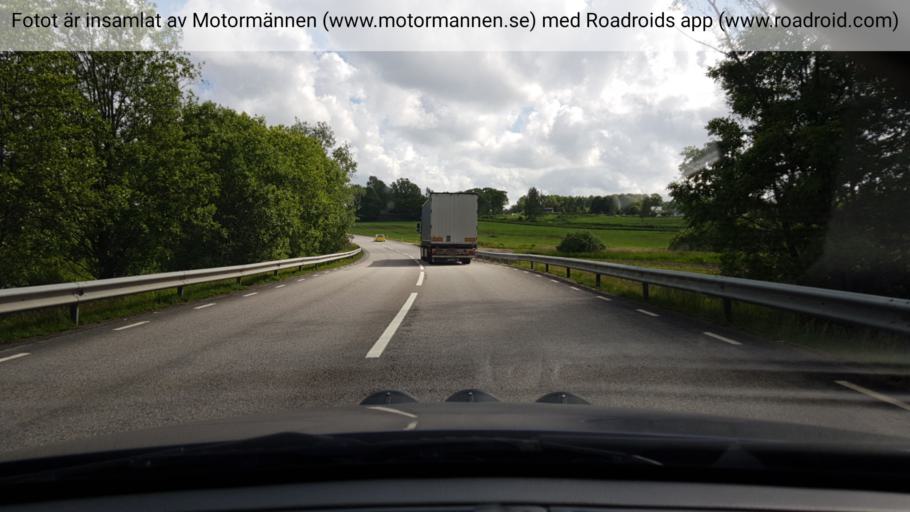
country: SE
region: Vaestra Goetaland
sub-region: Marks Kommun
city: Horred
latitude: 57.3669
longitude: 12.4824
